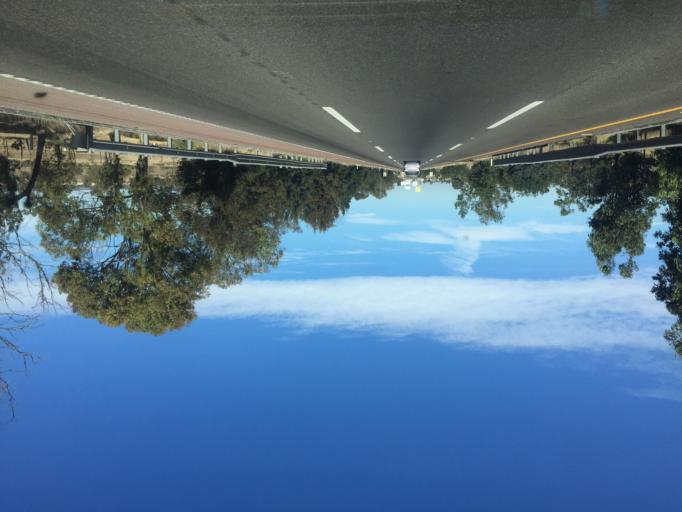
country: MX
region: Queretaro
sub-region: San Juan del Rio
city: El Cazadero
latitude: 20.2556
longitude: -99.8471
